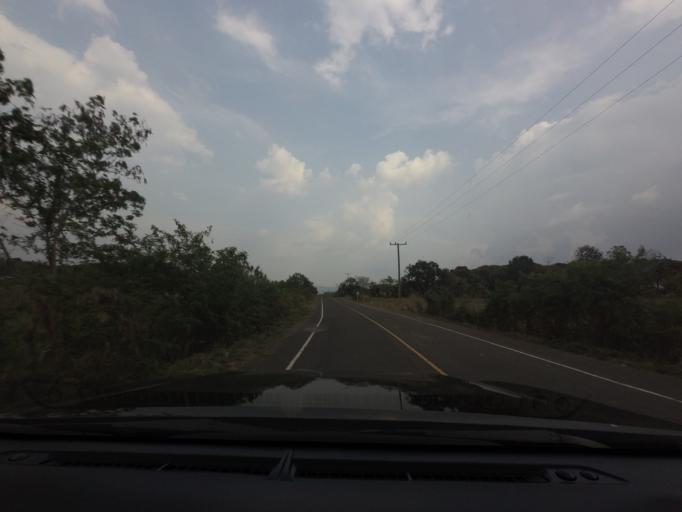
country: TH
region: Nakhon Ratchasima
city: Wang Nam Khiao
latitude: 14.4166
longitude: 101.7805
